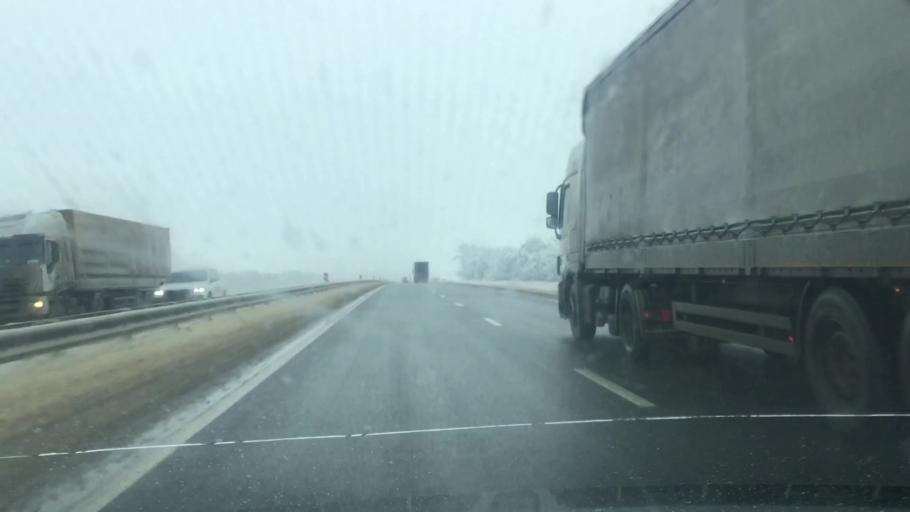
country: RU
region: Lipetsk
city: Stanovoye
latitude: 52.8941
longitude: 38.2337
